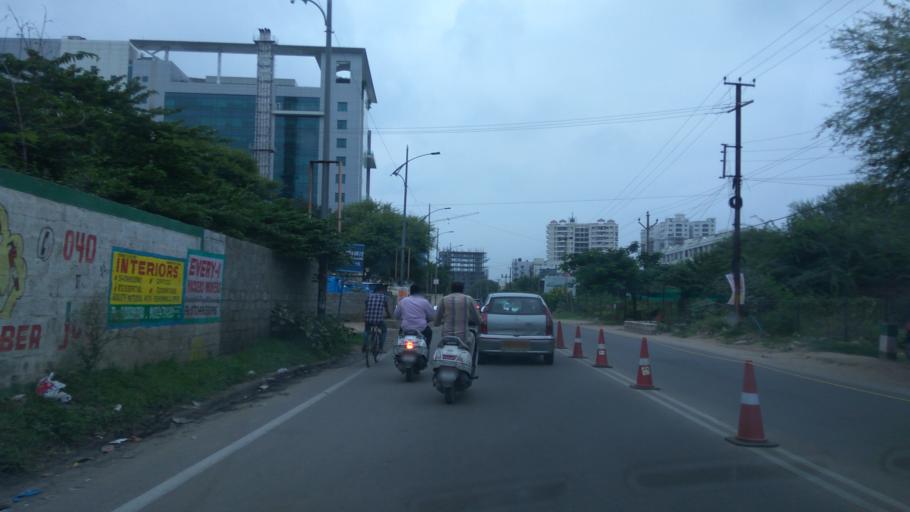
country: IN
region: Telangana
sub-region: Rangareddi
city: Kukatpalli
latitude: 17.4348
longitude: 78.3883
